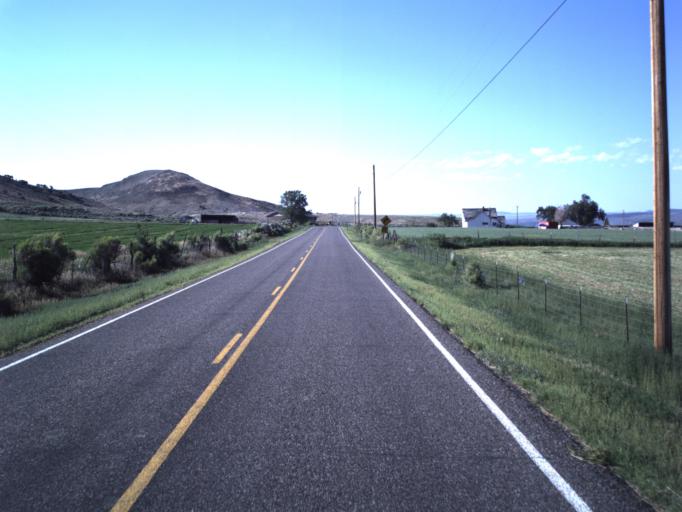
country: US
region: Utah
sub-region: Wayne County
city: Loa
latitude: 38.4431
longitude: -111.6158
